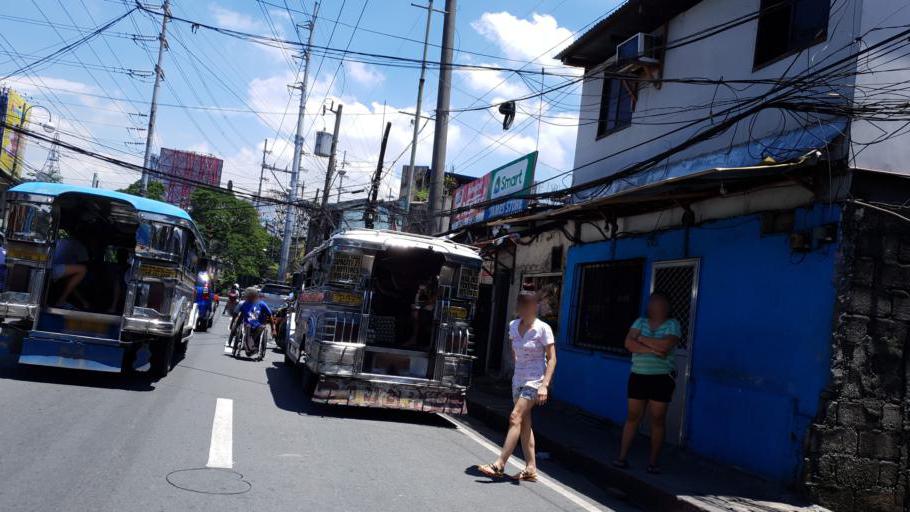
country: PH
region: Calabarzon
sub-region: Province of Rizal
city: Pateros
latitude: 14.5602
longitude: 121.0639
